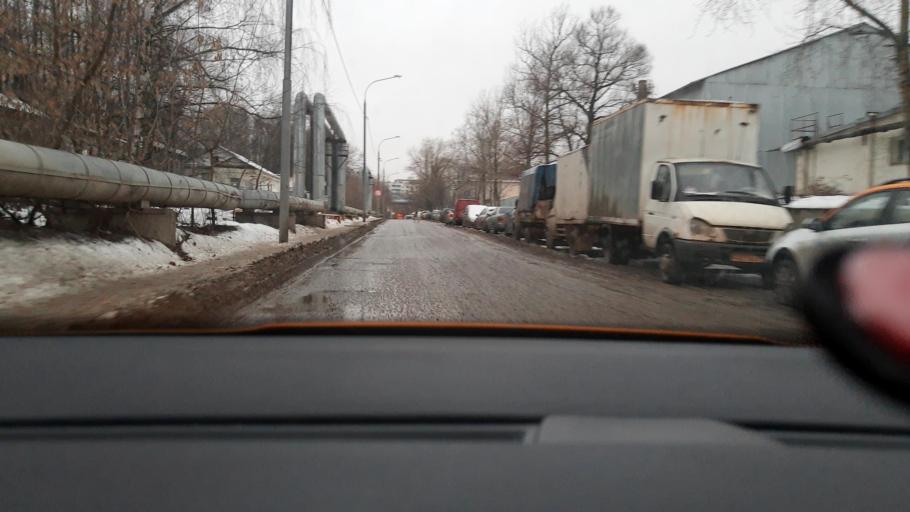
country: RU
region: Moscow
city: Zapadnoye Degunino
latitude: 55.8499
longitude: 37.5304
